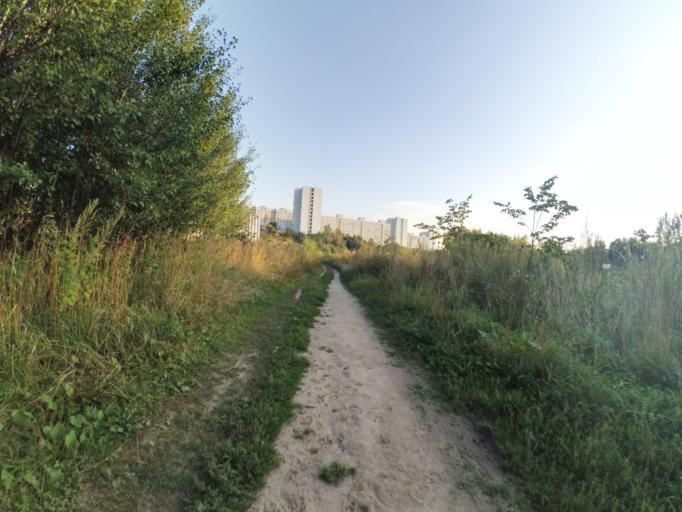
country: RU
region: Moscow
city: Khimki
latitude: 55.8626
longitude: 37.4105
